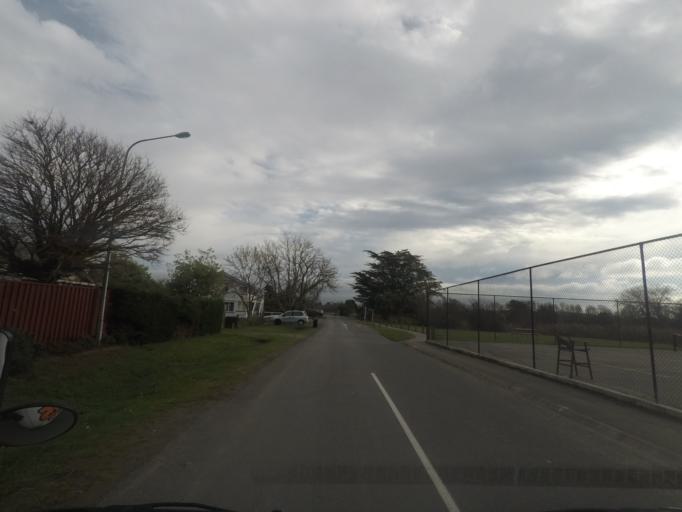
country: NZ
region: Canterbury
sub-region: Waimakariri District
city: Woodend
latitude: -43.2882
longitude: 172.7177
